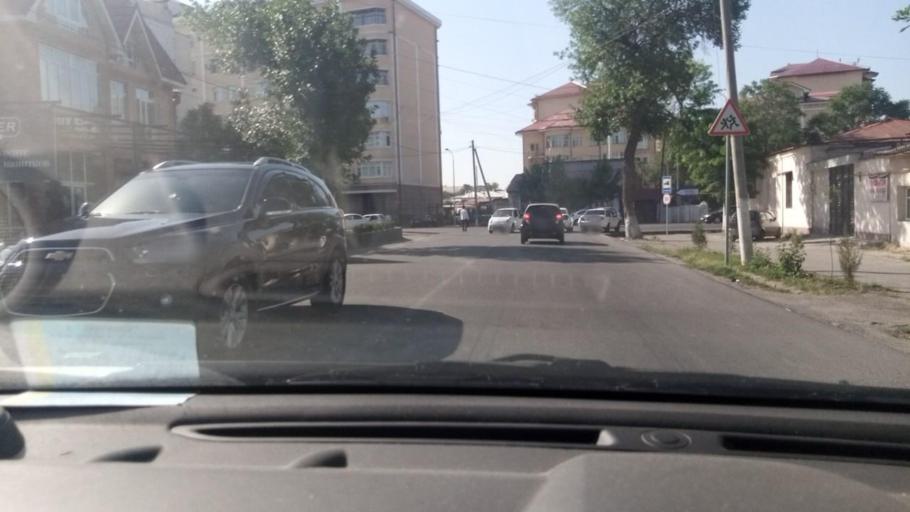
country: UZ
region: Toshkent Shahri
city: Tashkent
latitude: 41.2812
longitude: 69.2856
